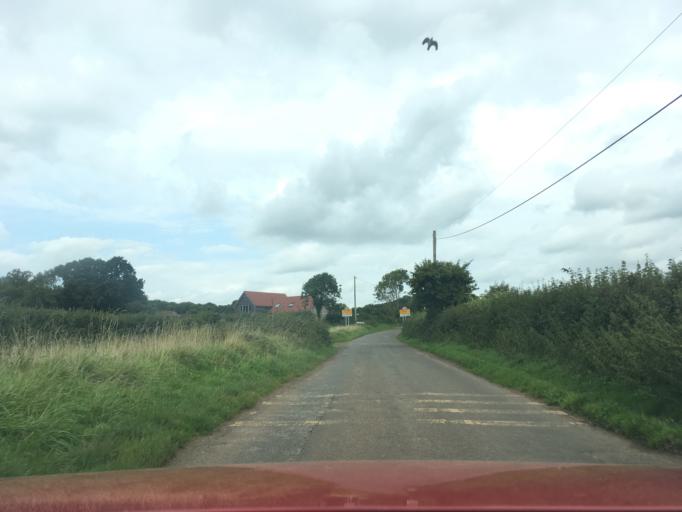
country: GB
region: England
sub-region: South Gloucestershire
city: Tytherington
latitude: 51.5883
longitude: -2.4824
